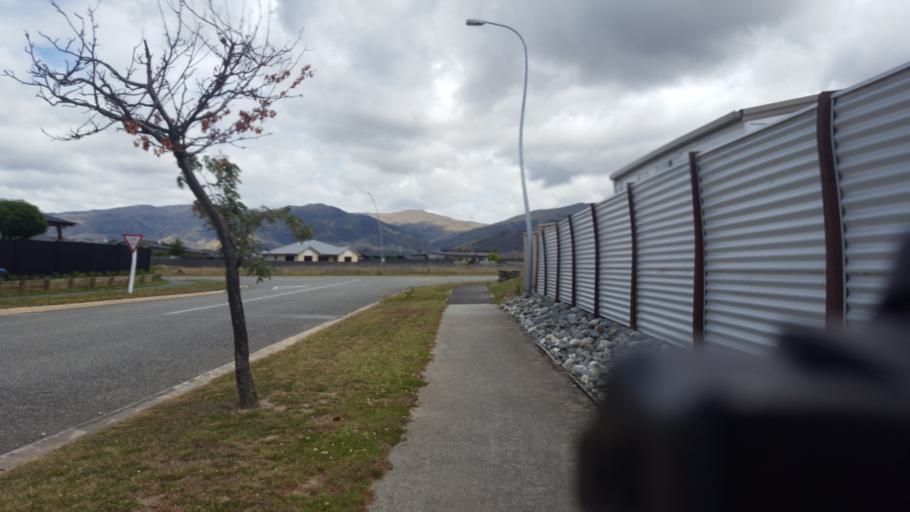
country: NZ
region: Otago
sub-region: Queenstown-Lakes District
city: Wanaka
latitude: -45.0442
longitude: 169.1809
